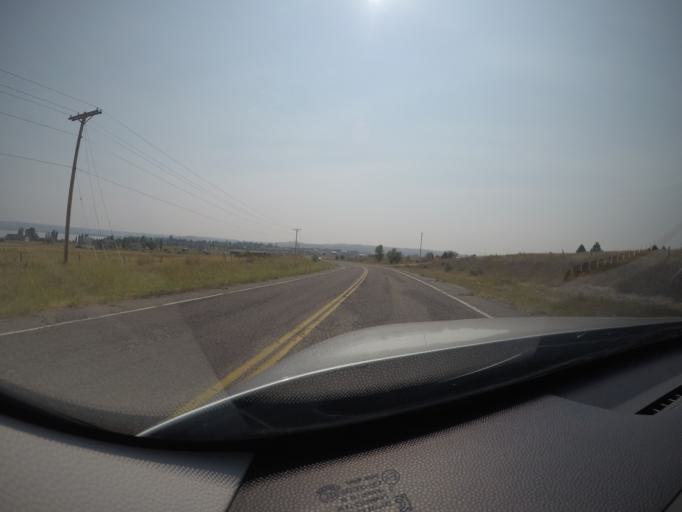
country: US
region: Montana
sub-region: Lake County
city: Polson
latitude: 47.7352
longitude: -114.1871
